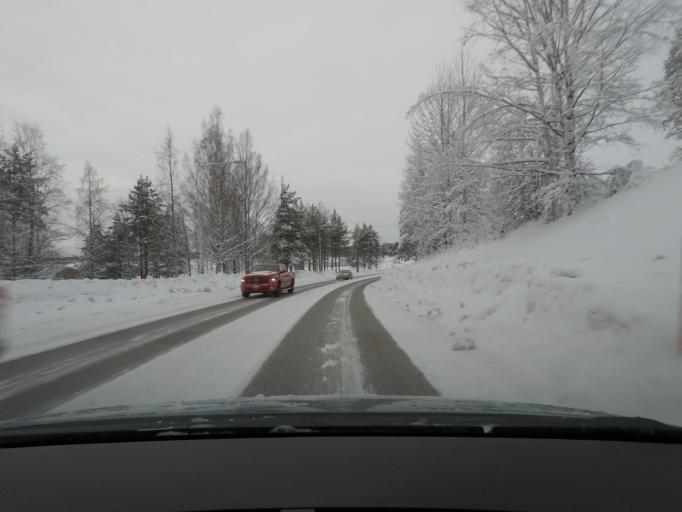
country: SE
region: Norrbotten
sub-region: Lulea Kommun
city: Lulea
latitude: 65.5912
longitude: 22.1844
